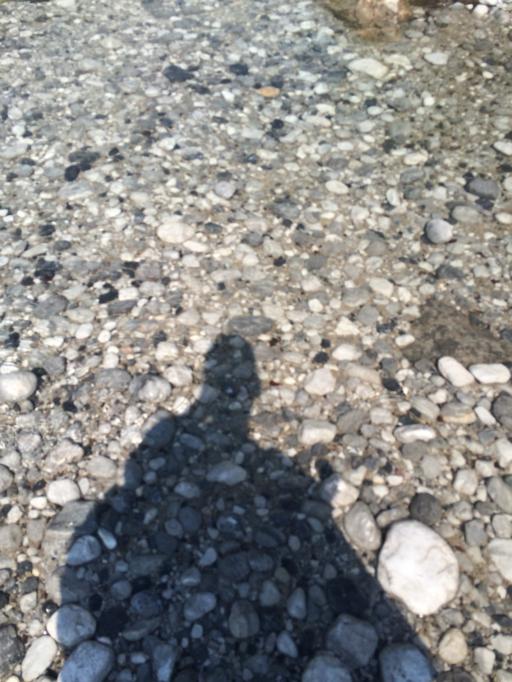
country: AL
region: Shkoder
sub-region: Rrethi i Shkodres
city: Nicaj-Shale
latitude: 42.3554
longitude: 19.7667
